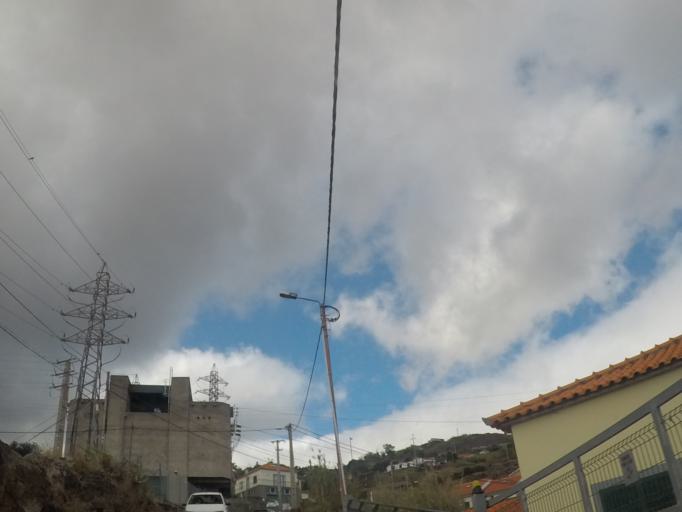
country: PT
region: Madeira
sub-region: Santa Cruz
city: Camacha
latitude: 32.6601
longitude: -16.8278
